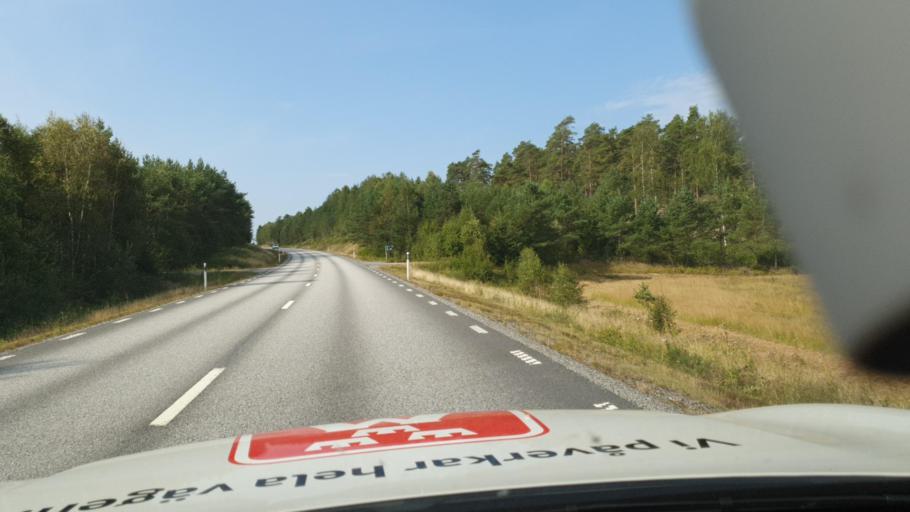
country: SE
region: Vaestra Goetaland
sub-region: Dals-Ed Kommun
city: Ed
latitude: 58.8489
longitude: 11.6847
